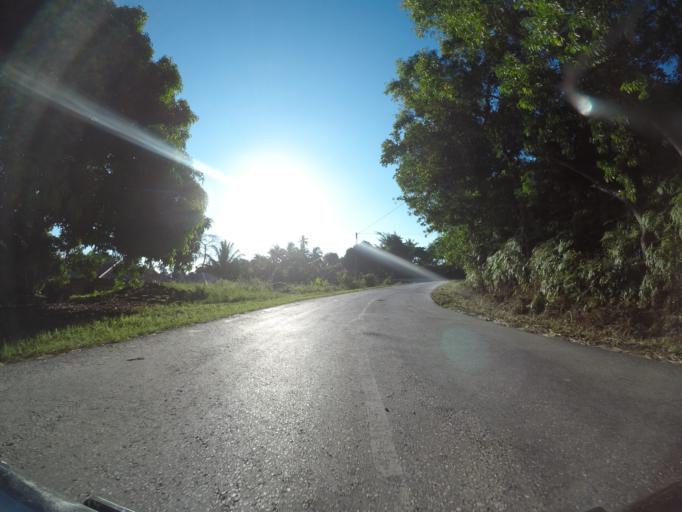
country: TZ
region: Pemba South
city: Mtambile
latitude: -5.3783
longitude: 39.6875
